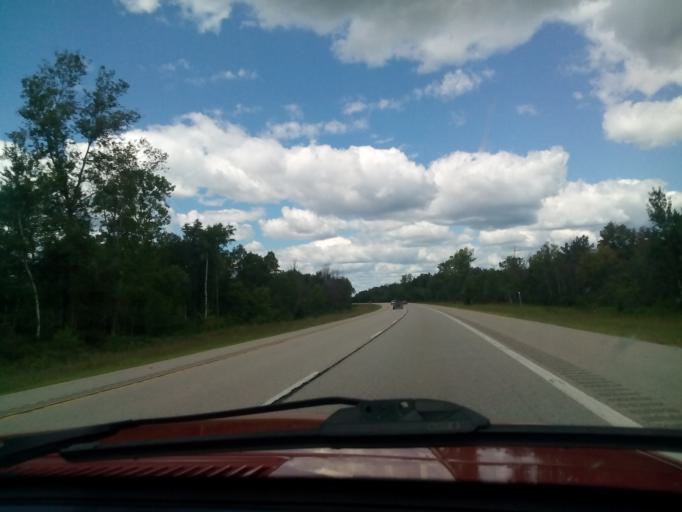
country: US
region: Michigan
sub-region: Ogemaw County
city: Skidway Lake
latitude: 44.0724
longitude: -84.0913
